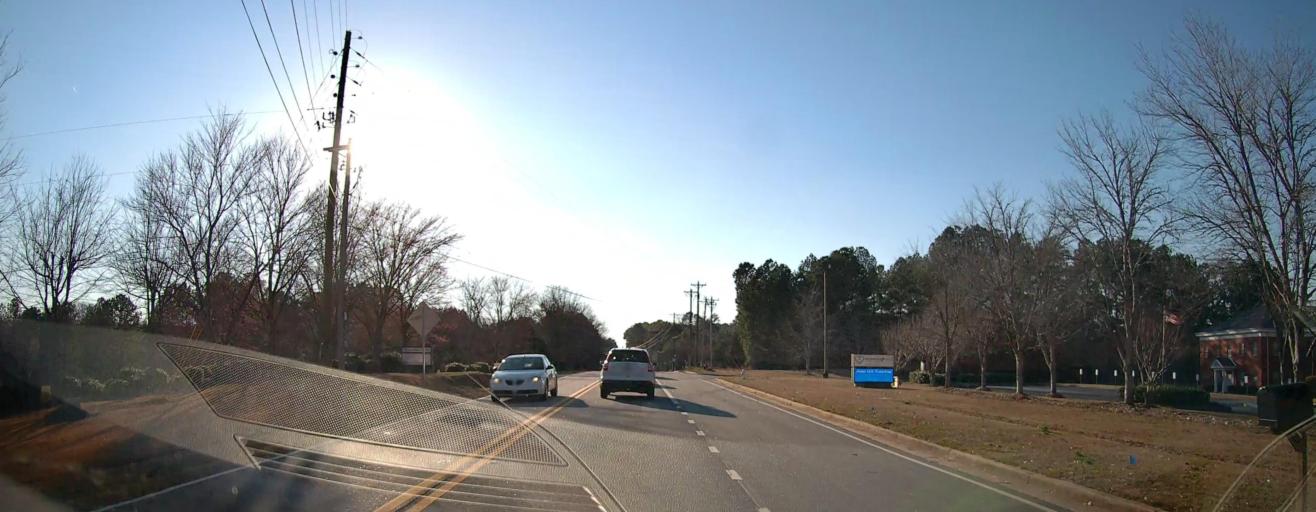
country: US
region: Georgia
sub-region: Clayton County
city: Irondale
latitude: 33.4582
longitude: -84.4006
